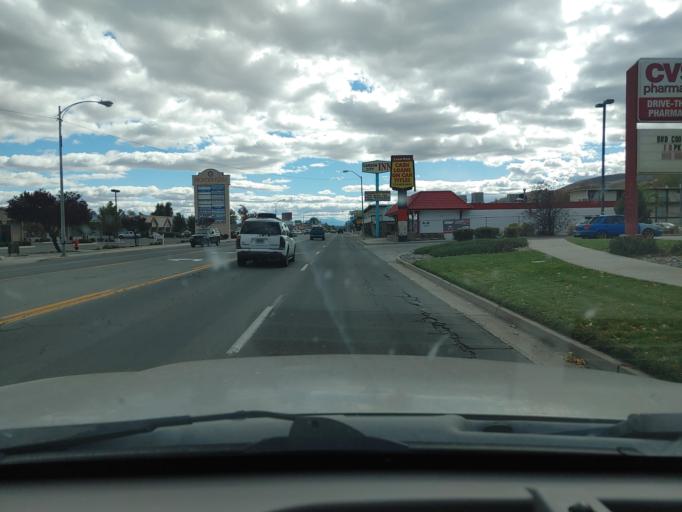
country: US
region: Nevada
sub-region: Carson City
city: Carson City
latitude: 39.1786
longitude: -119.7670
